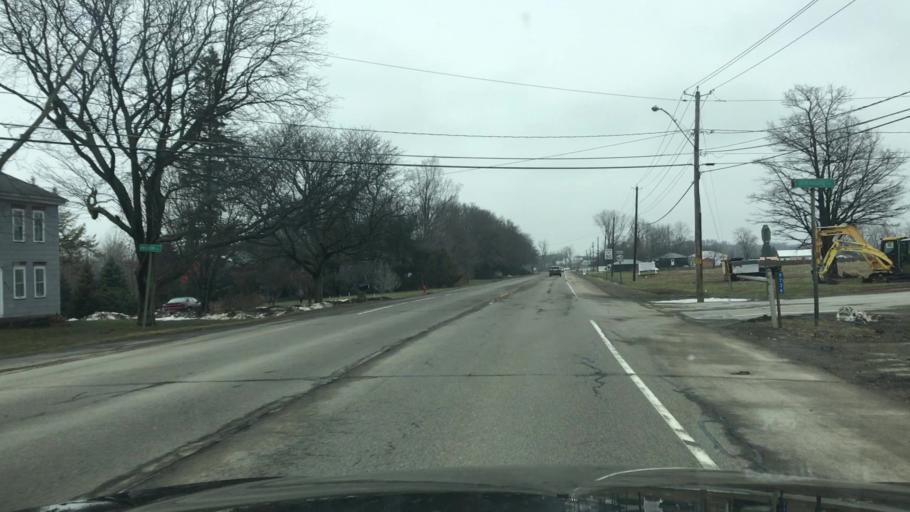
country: US
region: New York
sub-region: Chautauqua County
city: Fredonia
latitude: 42.4256
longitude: -79.3062
